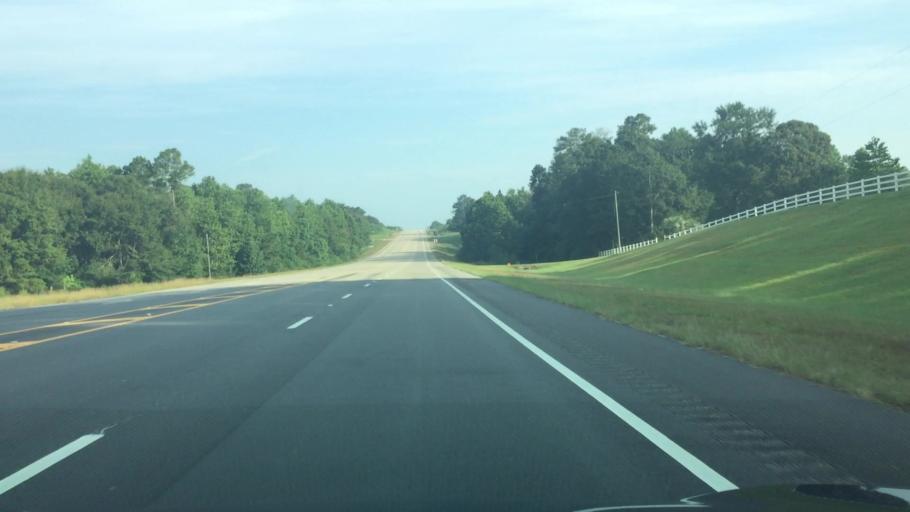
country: US
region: Alabama
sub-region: Butler County
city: Georgiana
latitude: 31.5336
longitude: -86.7232
